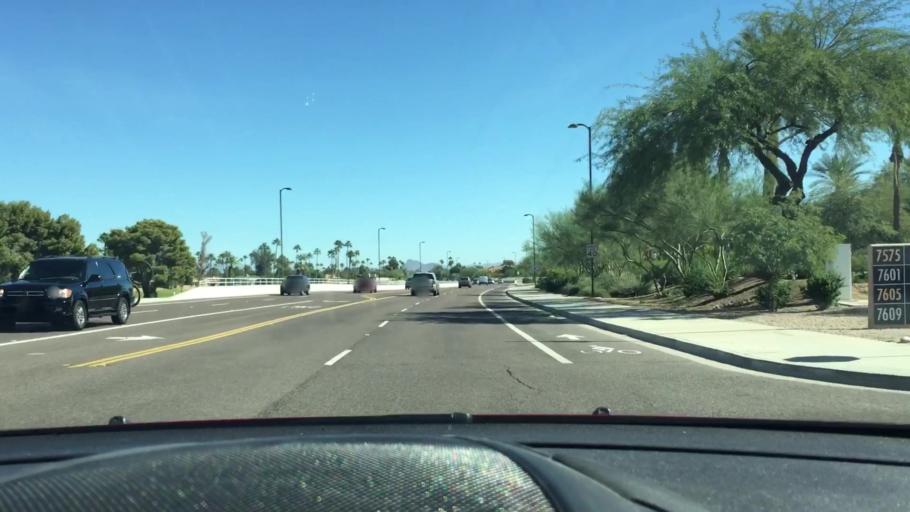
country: US
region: Arizona
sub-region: Maricopa County
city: Paradise Valley
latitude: 33.5385
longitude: -111.9192
